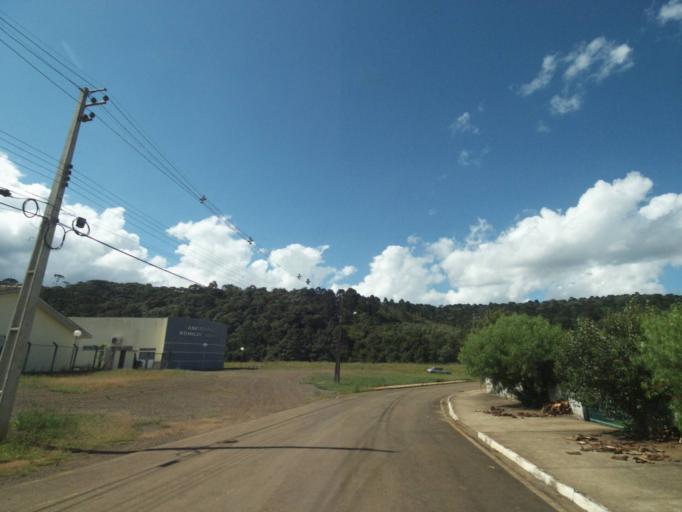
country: BR
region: Parana
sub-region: Uniao Da Vitoria
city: Uniao da Vitoria
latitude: -26.1508
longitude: -51.5475
